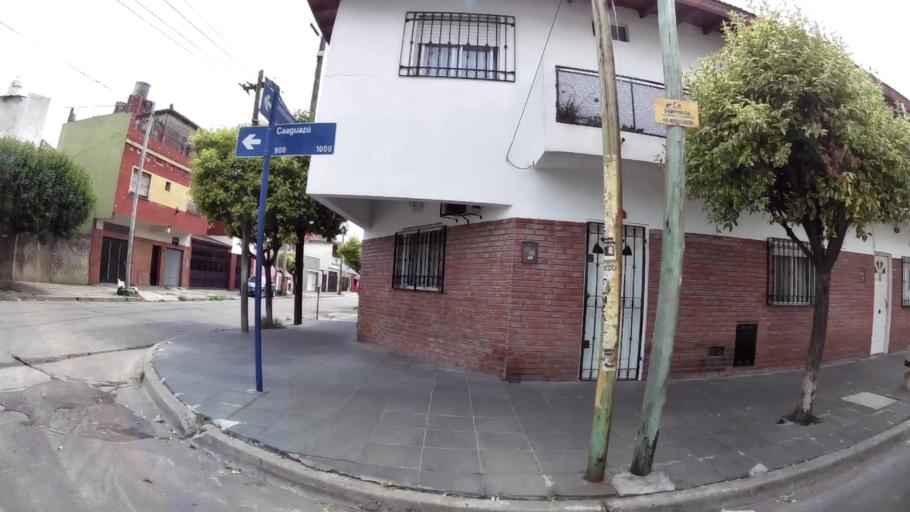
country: AR
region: Buenos Aires F.D.
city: Villa Lugano
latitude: -34.6860
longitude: -58.5031
